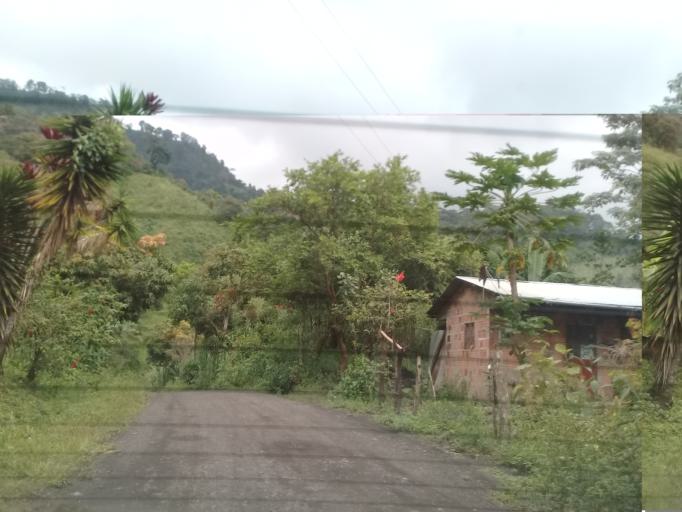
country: CO
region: Cundinamarca
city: Quipile
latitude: 4.7184
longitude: -74.5446
